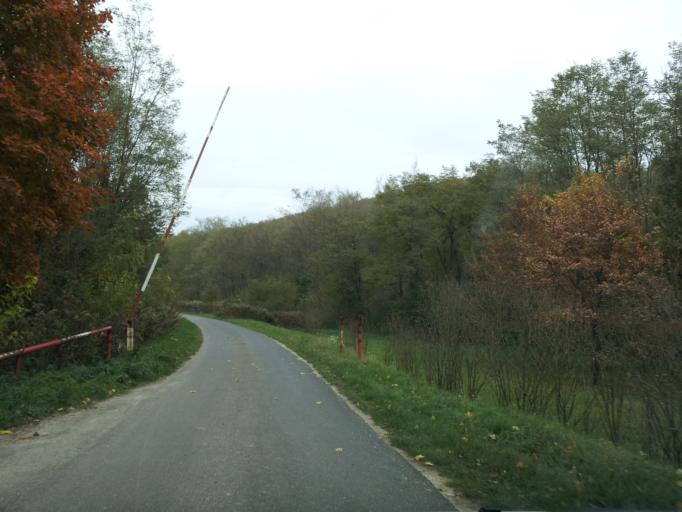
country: HU
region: Gyor-Moson-Sopron
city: Pannonhalma
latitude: 47.4768
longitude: 17.7127
